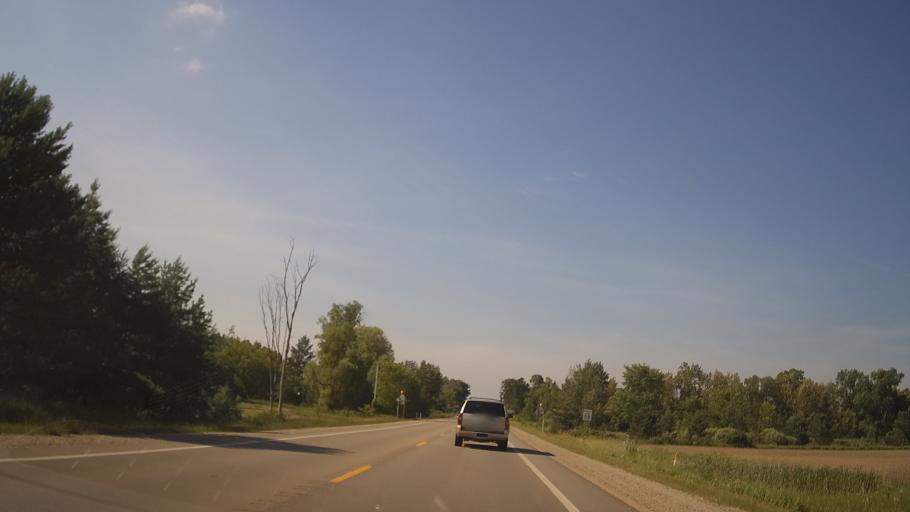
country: US
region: Michigan
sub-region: Ogemaw County
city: West Branch
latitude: 44.2793
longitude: -84.1257
